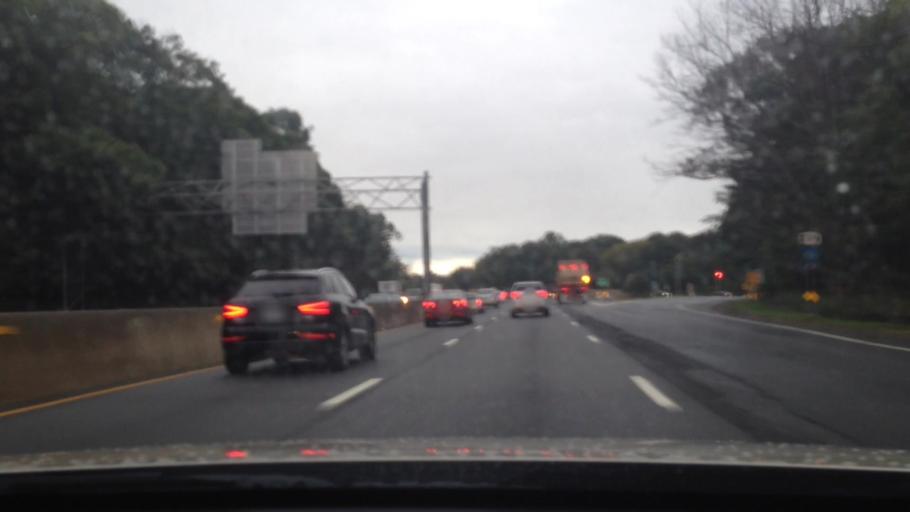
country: US
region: New York
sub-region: Suffolk County
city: North Great River
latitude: 40.7483
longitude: -73.1560
